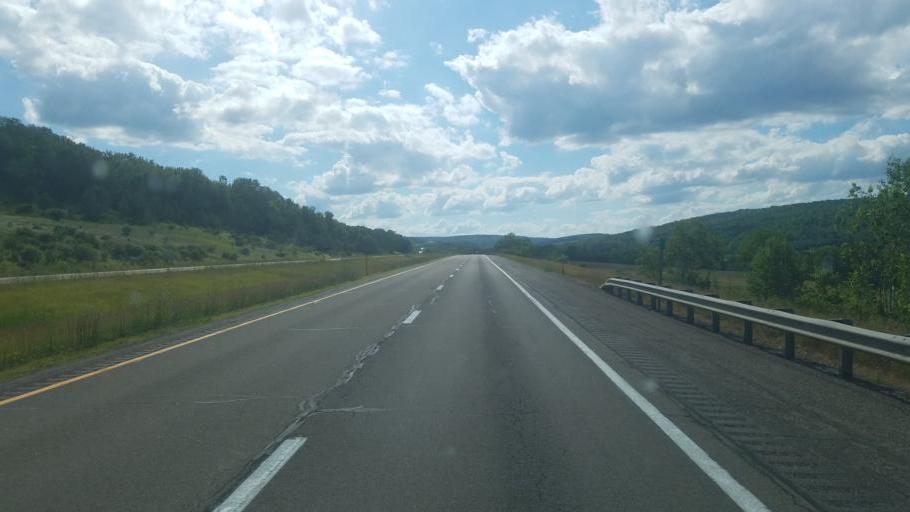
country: US
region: New York
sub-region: Allegany County
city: Alfred
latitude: 42.3172
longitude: -77.7928
